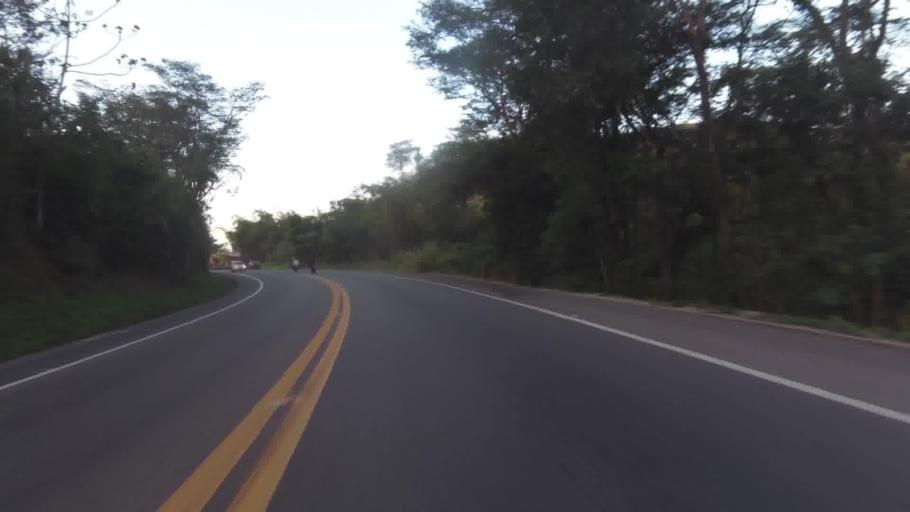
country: BR
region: Espirito Santo
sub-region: Iconha
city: Iconha
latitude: -20.7866
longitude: -40.7827
